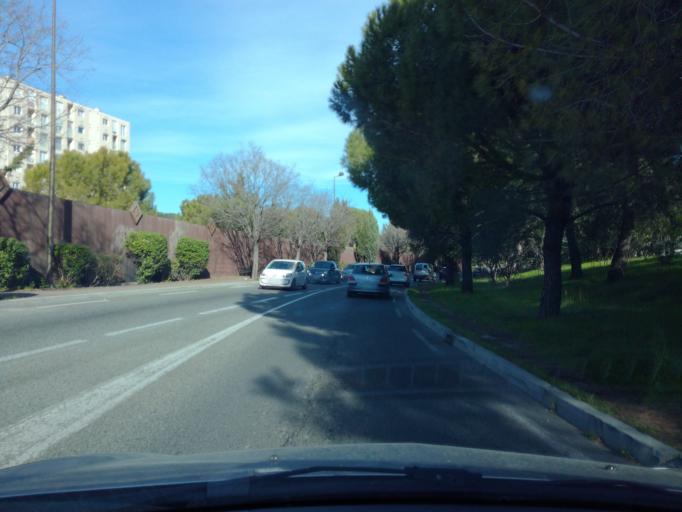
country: FR
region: Provence-Alpes-Cote d'Azur
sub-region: Departement des Alpes-Maritimes
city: Vallauris
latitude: 43.5768
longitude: 7.0903
